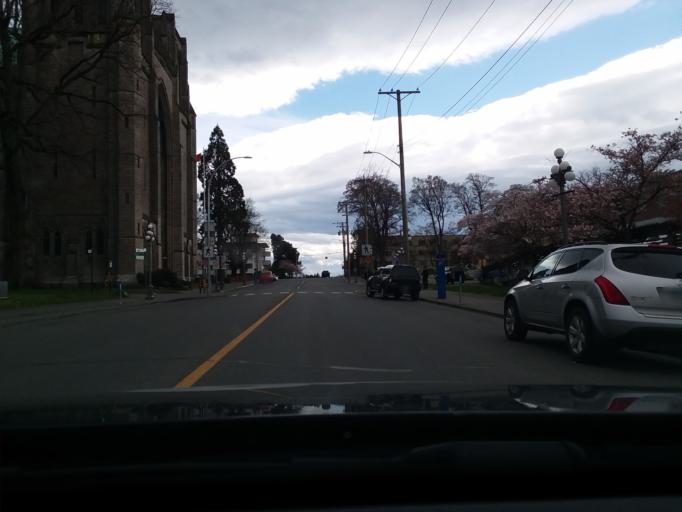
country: CA
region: British Columbia
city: Victoria
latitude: 48.4230
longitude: -123.3600
